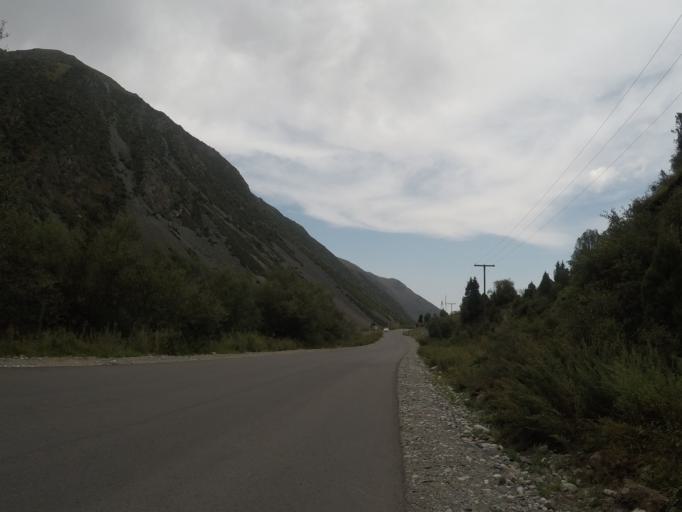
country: KG
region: Chuy
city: Bishkek
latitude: 42.5773
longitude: 74.4817
